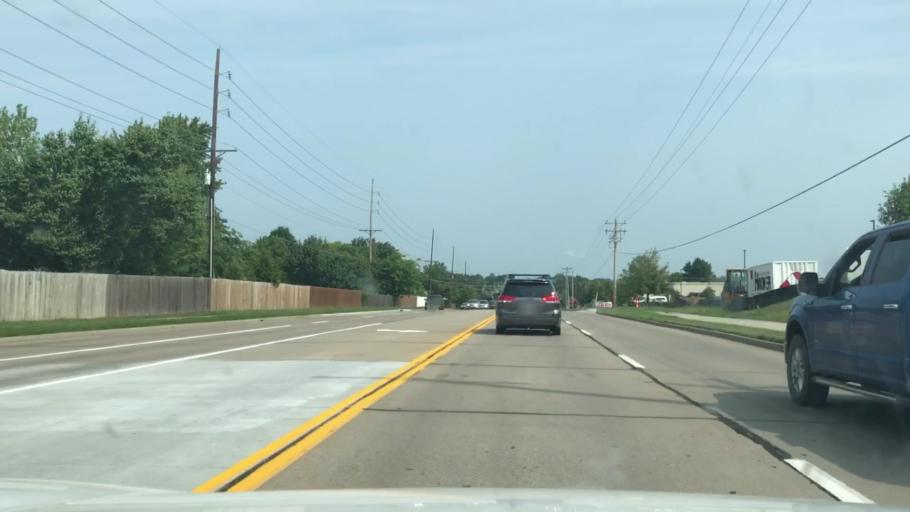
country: US
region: Missouri
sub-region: Saint Charles County
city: Dardenne Prairie
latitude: 38.7850
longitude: -90.7370
